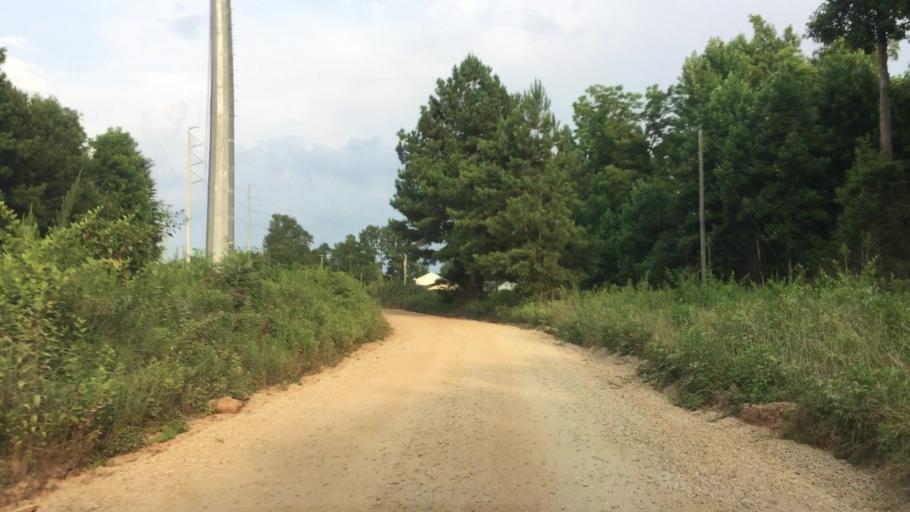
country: US
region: Georgia
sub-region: Henry County
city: McDonough
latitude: 33.5277
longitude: -84.1270
